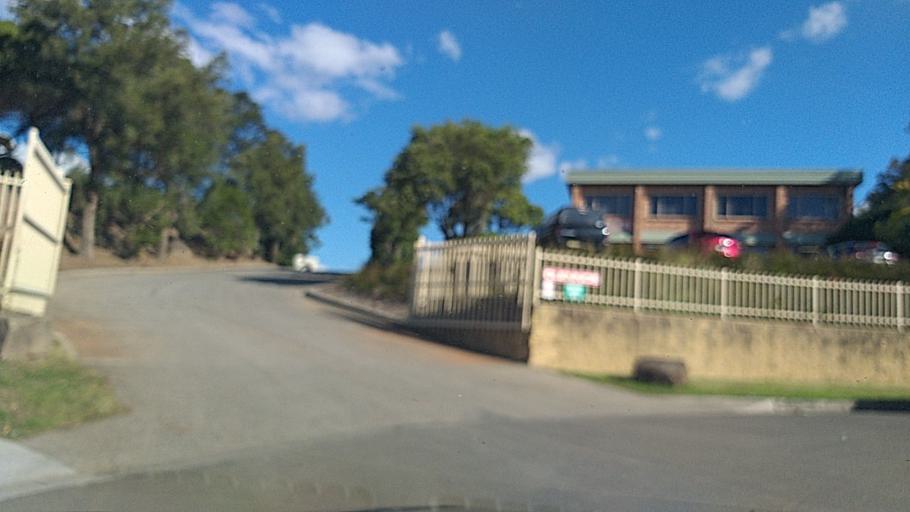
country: AU
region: New South Wales
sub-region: Wollongong
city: Berkeley
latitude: -34.4699
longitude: 150.8340
